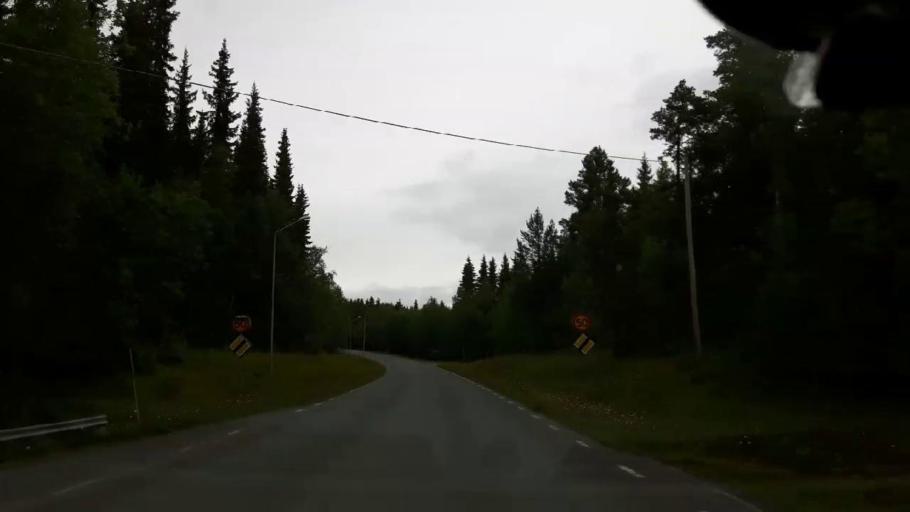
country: SE
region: Jaemtland
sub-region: Krokoms Kommun
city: Valla
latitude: 63.6471
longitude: 13.8300
